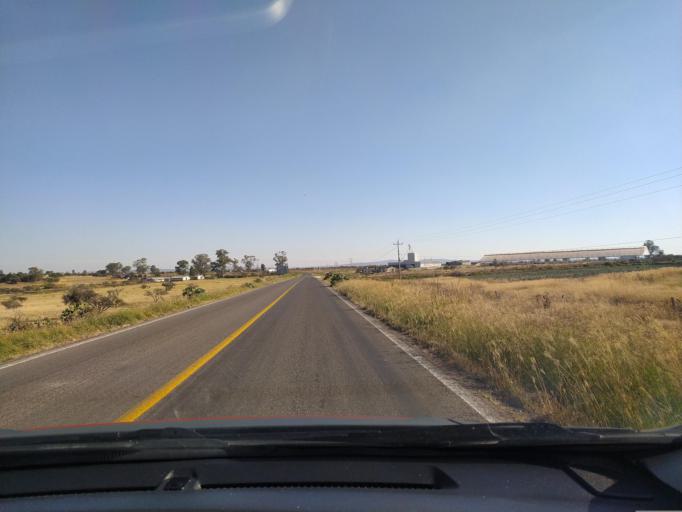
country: MX
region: Jalisco
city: Valle de Guadalupe
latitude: 21.0268
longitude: -102.5490
